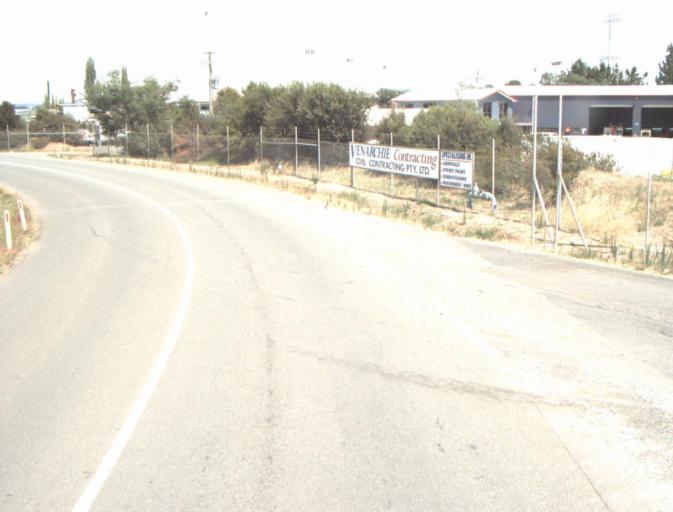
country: AU
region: Tasmania
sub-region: Launceston
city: Newnham
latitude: -41.4019
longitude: 147.1474
